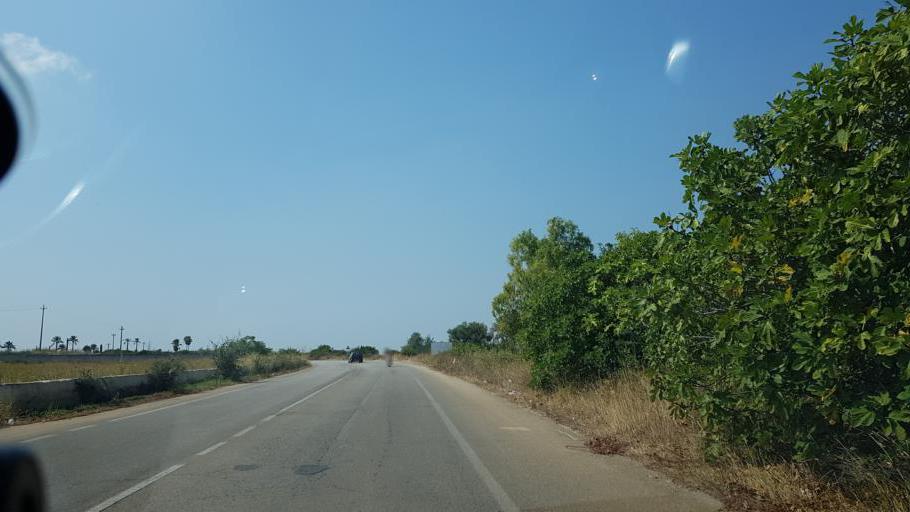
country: IT
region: Apulia
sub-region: Provincia di Taranto
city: Uggiano Montefusco
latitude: 40.3557
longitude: 17.6006
